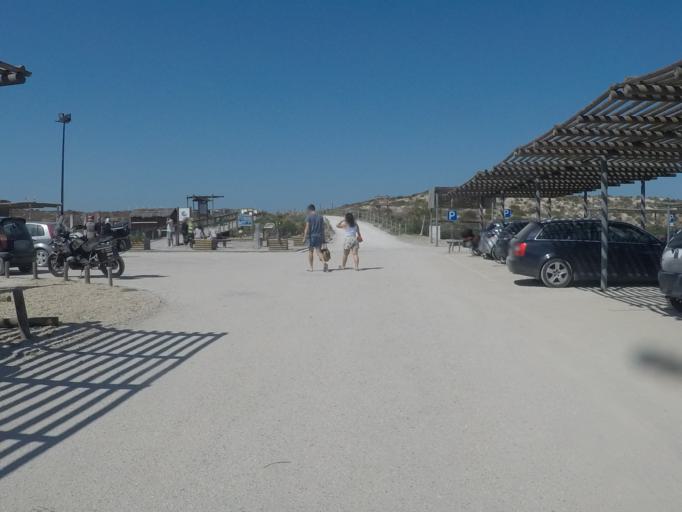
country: PT
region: Setubal
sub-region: Setubal
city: Setubal
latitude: 38.3822
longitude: -8.8013
